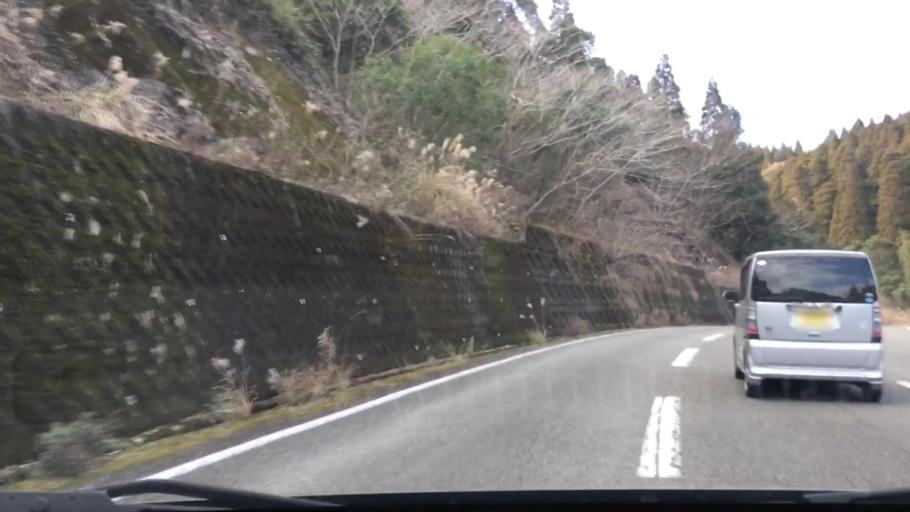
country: JP
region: Miyazaki
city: Nichinan
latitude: 31.6305
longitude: 131.3391
